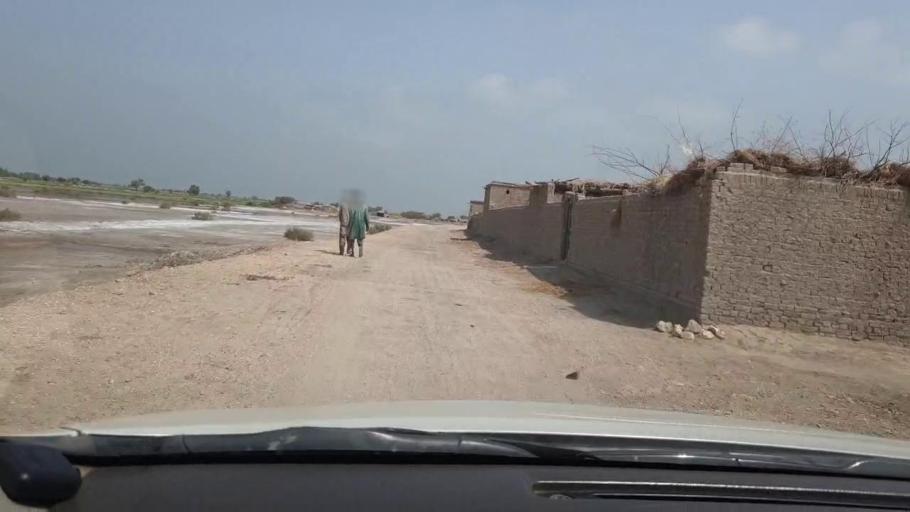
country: PK
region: Sindh
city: Shikarpur
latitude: 28.0025
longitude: 68.5580
